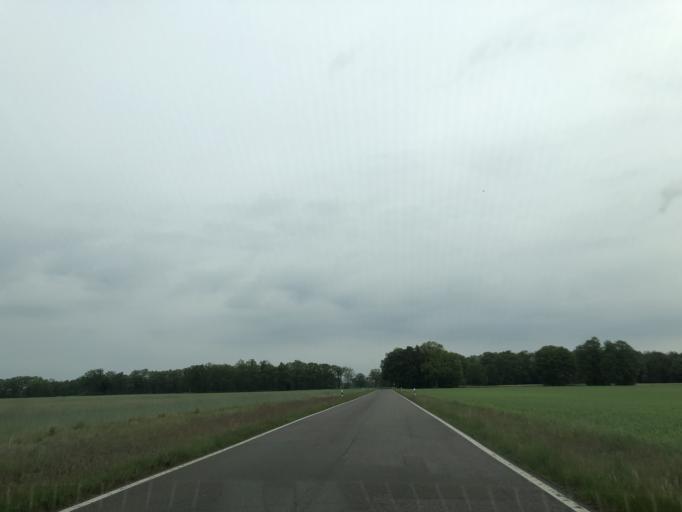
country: DE
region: Brandenburg
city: Plattenburg
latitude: 52.9490
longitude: 12.1190
